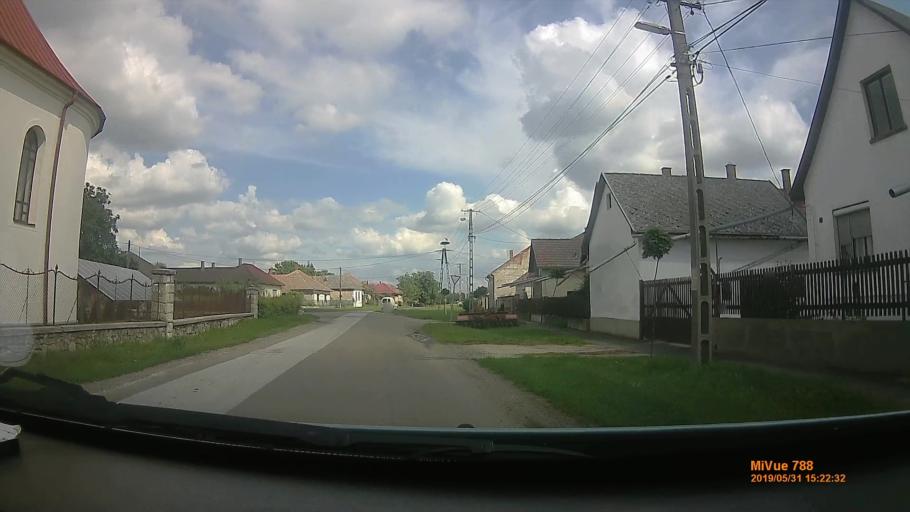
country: HU
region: Borsod-Abauj-Zemplen
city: Taktaharkany
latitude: 48.0826
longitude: 21.1398
